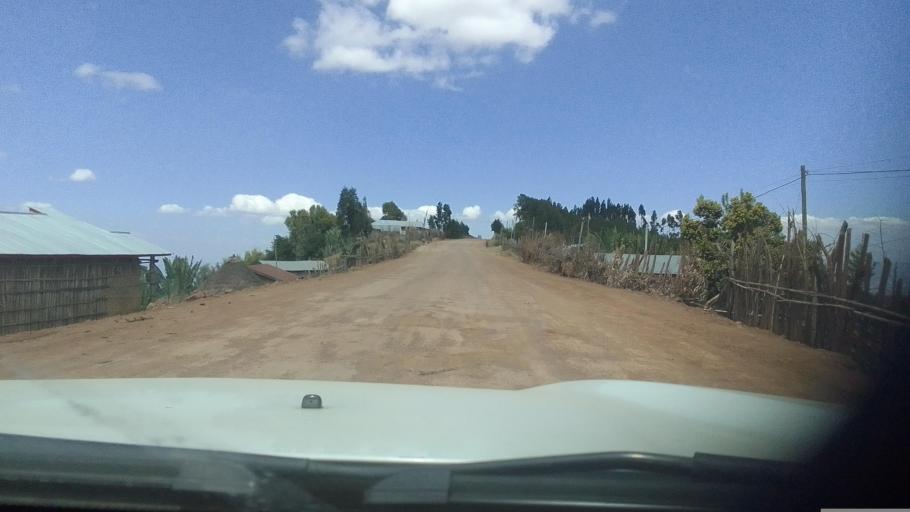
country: ET
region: Oromiya
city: Hagere Hiywet
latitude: 8.8393
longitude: 37.8858
